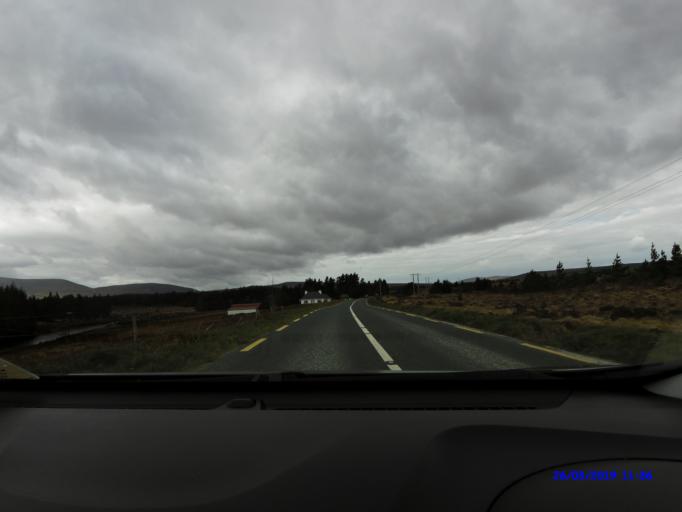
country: IE
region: Connaught
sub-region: Maigh Eo
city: Crossmolina
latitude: 54.1219
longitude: -9.5972
